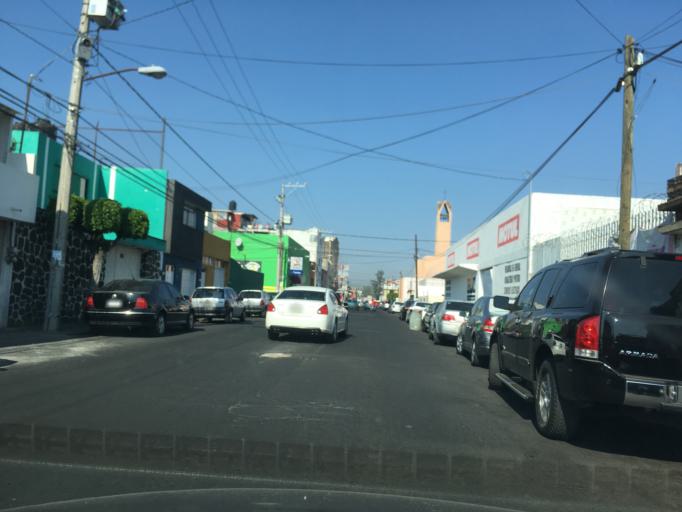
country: MX
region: Michoacan
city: Morelia
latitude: 19.7010
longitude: -101.2091
